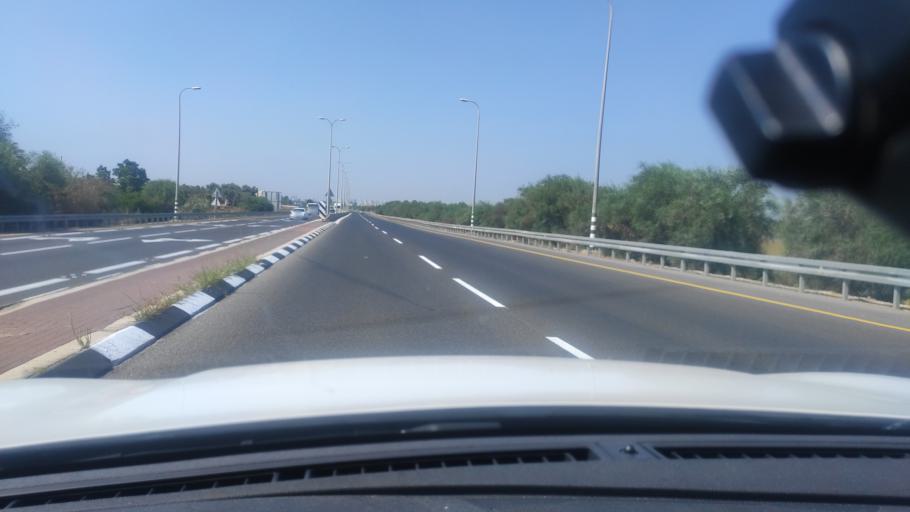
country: IL
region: Central District
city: Kfar Saba
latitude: 32.1505
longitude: 34.9206
